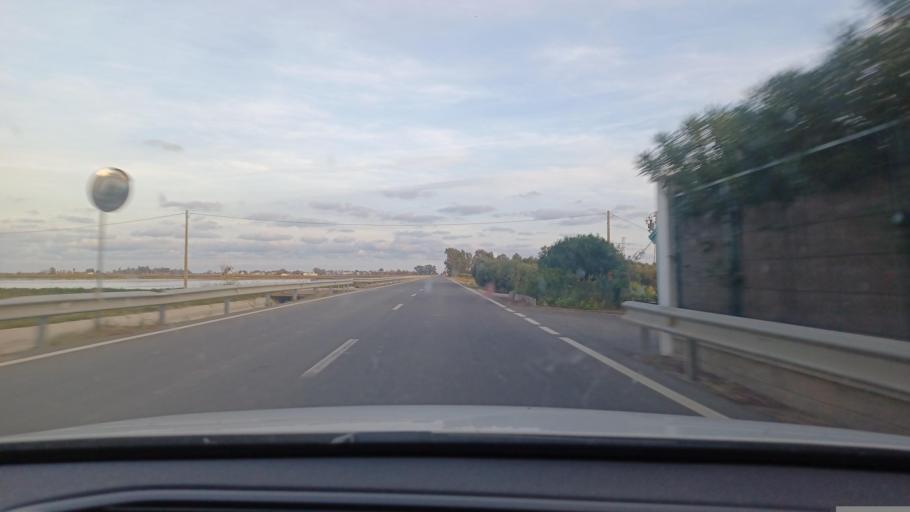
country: ES
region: Catalonia
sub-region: Provincia de Tarragona
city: Deltebre
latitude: 40.6638
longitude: 0.7598
